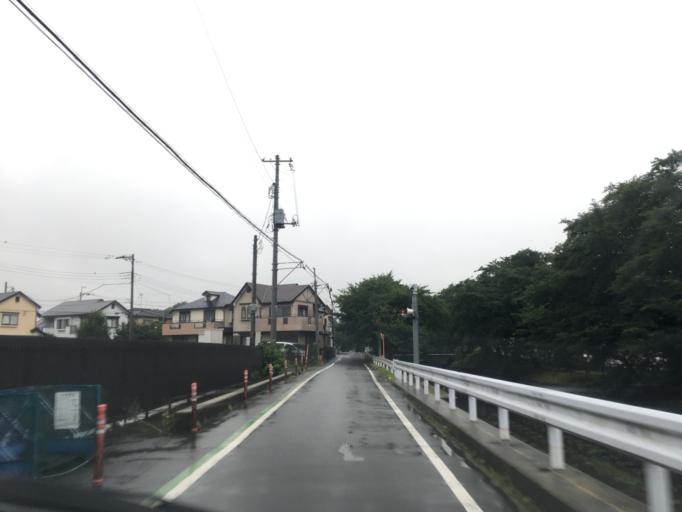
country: JP
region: Saitama
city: Tokorozawa
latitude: 35.7943
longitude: 139.4857
